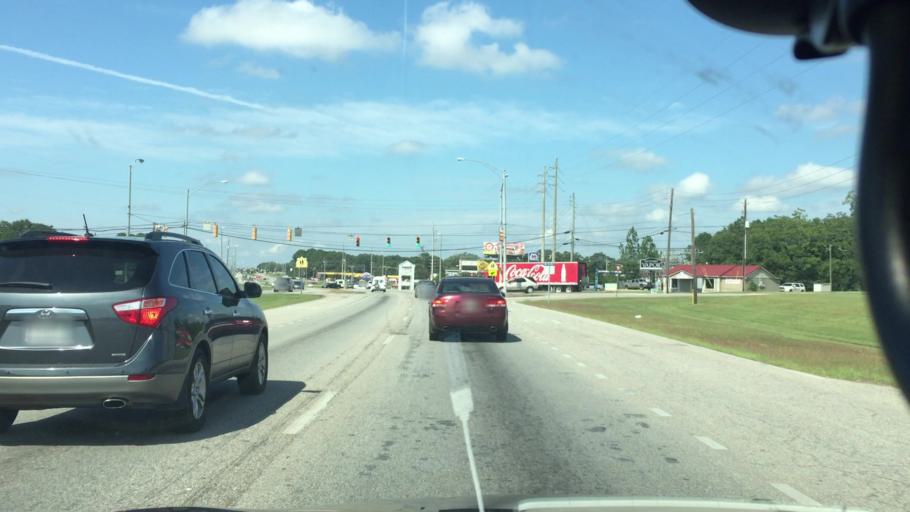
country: US
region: Alabama
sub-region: Coffee County
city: Enterprise
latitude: 31.3350
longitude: -85.8529
